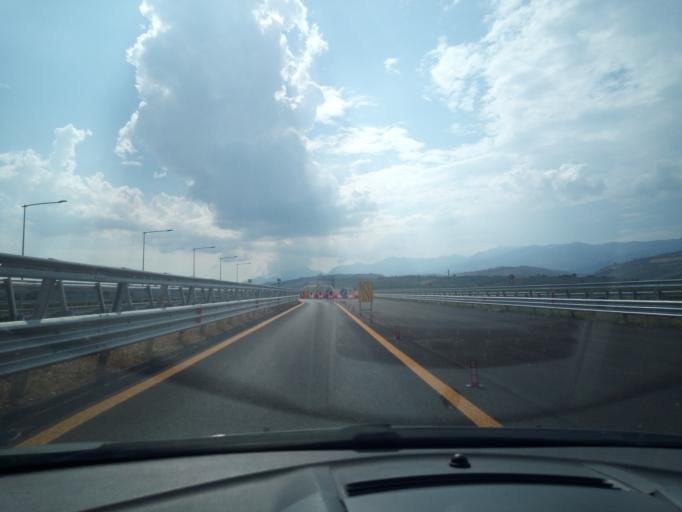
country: IT
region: Calabria
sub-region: Provincia di Cosenza
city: San Lorenzo del Vallo
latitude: 39.7228
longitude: 16.2501
